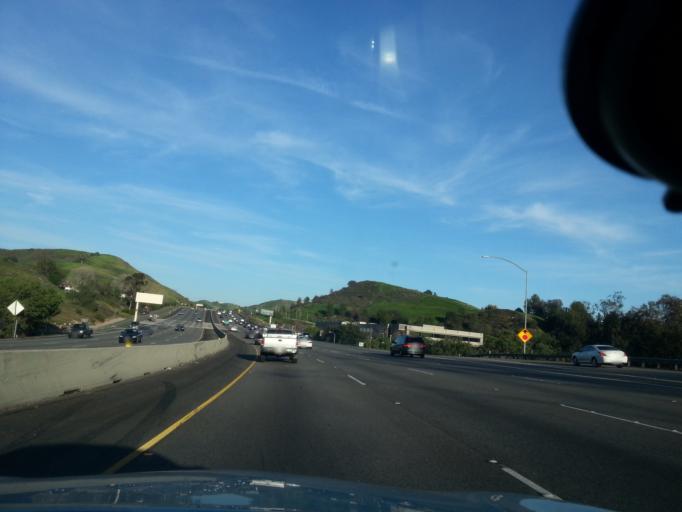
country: US
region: California
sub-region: Los Angeles County
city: Agoura
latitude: 34.1379
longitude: -118.7269
